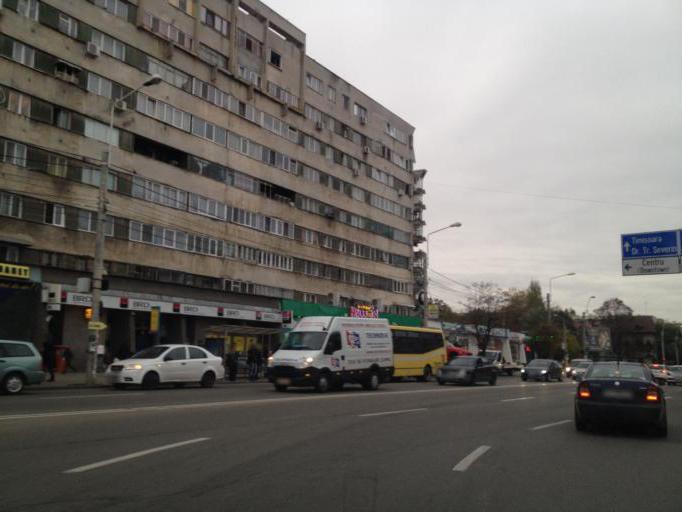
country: RO
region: Dolj
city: Craiova
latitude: 44.3277
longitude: 23.8163
